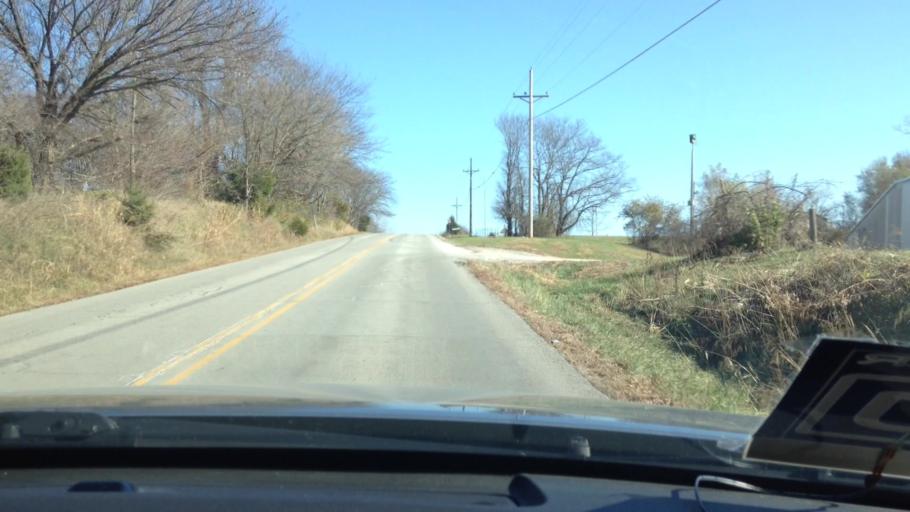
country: US
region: Missouri
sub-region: Platte County
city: Weston
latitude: 39.4177
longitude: -94.8896
